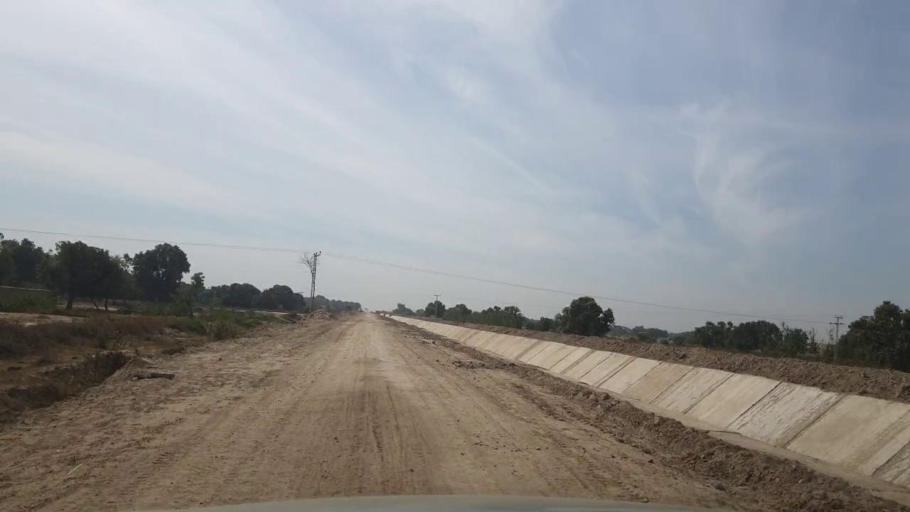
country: PK
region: Sindh
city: Kunri
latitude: 25.1483
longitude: 69.5884
